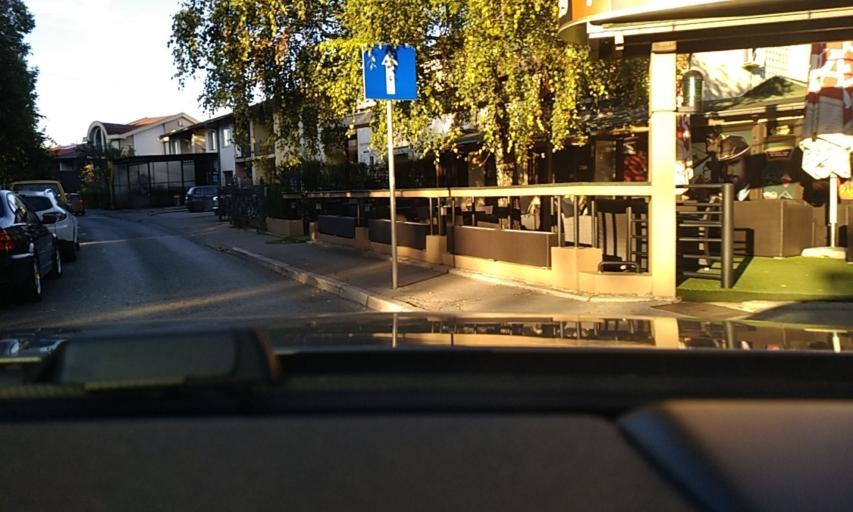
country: BA
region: Republika Srpska
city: Starcevica
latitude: 44.7686
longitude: 17.2087
